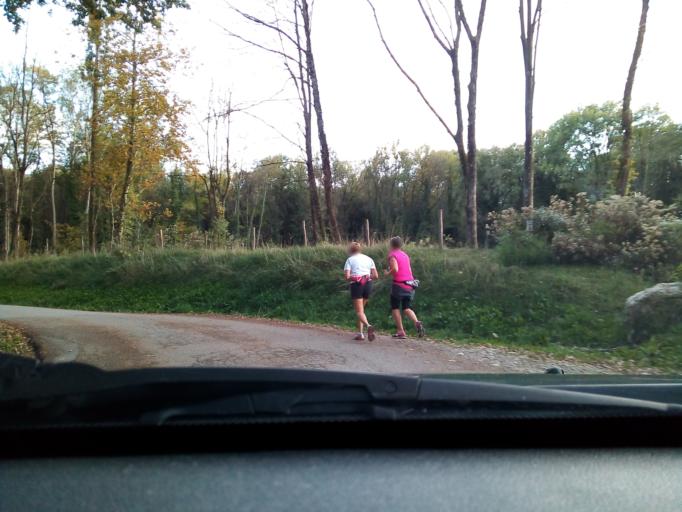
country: FR
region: Rhone-Alpes
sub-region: Departement de l'Isere
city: Domene
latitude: 45.2221
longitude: 5.8399
